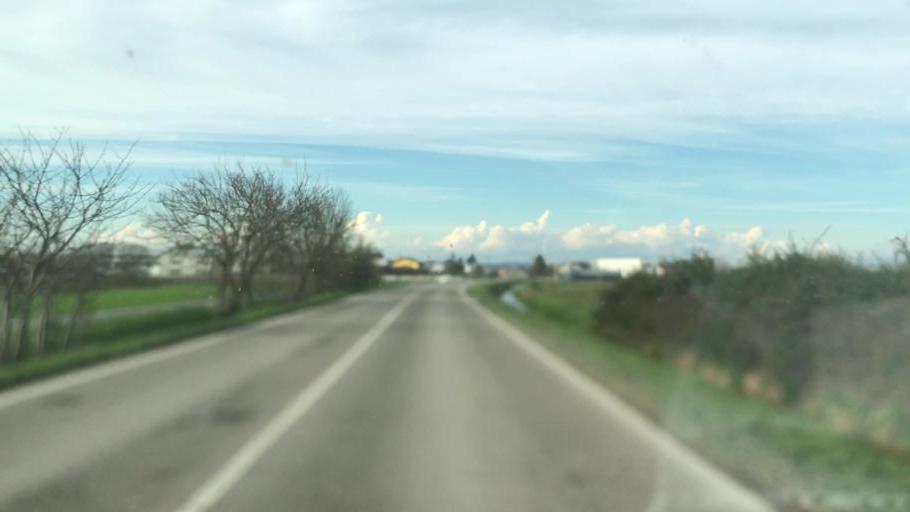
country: IT
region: Lombardy
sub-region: Provincia di Mantova
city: Cerlongo
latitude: 45.2713
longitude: 10.6610
